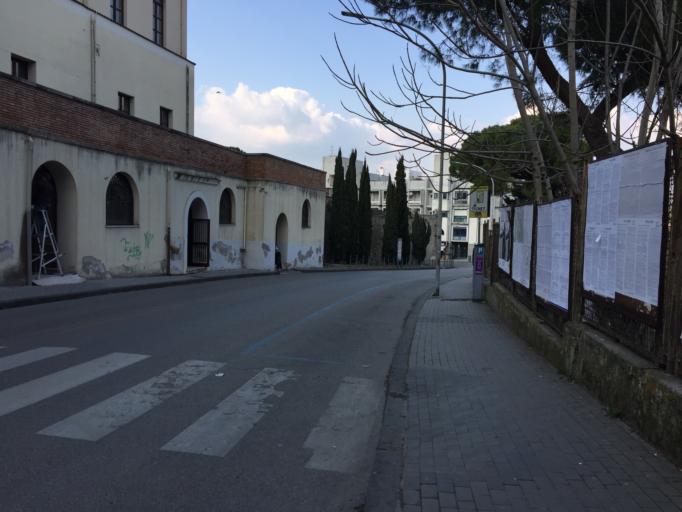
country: IT
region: Campania
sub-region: Provincia di Benevento
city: Benevento
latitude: 41.1310
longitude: 14.7826
